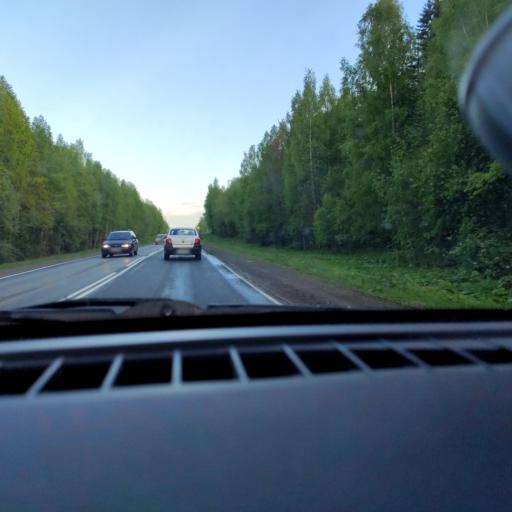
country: RU
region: Perm
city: Perm
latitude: 58.1486
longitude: 56.2592
